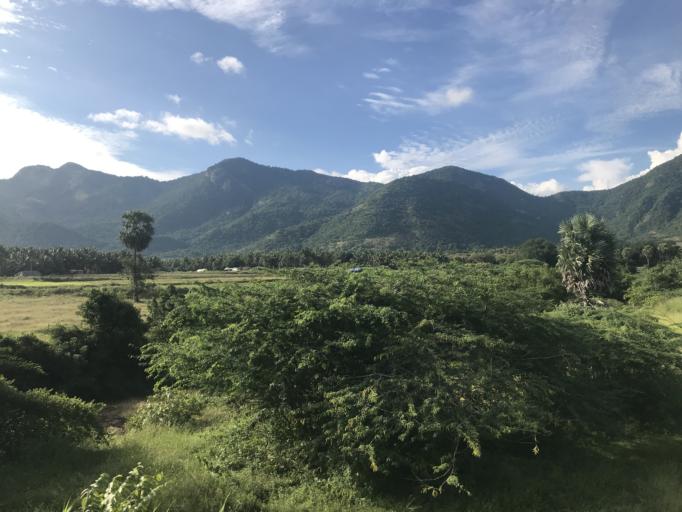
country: IN
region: Tamil Nadu
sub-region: Coimbatore
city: Madukkarai
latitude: 10.8873
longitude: 76.8775
